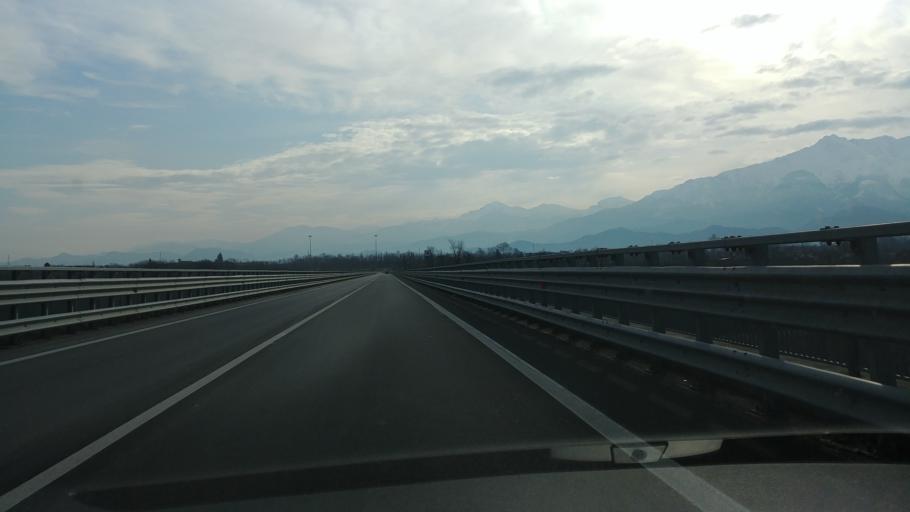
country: IT
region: Piedmont
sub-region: Provincia di Cuneo
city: Cuneo
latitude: 44.3716
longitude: 7.5453
